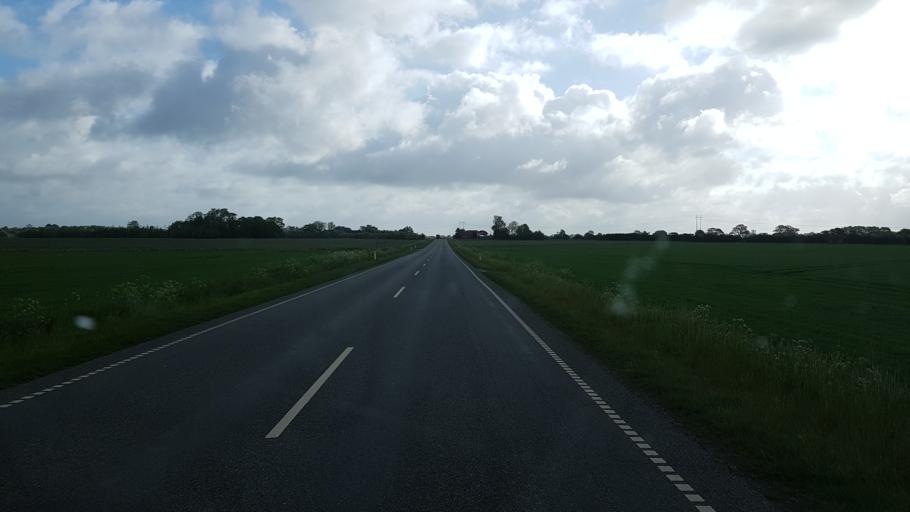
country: DK
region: South Denmark
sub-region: Vejen Kommune
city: Rodding
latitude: 55.4023
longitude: 9.1143
